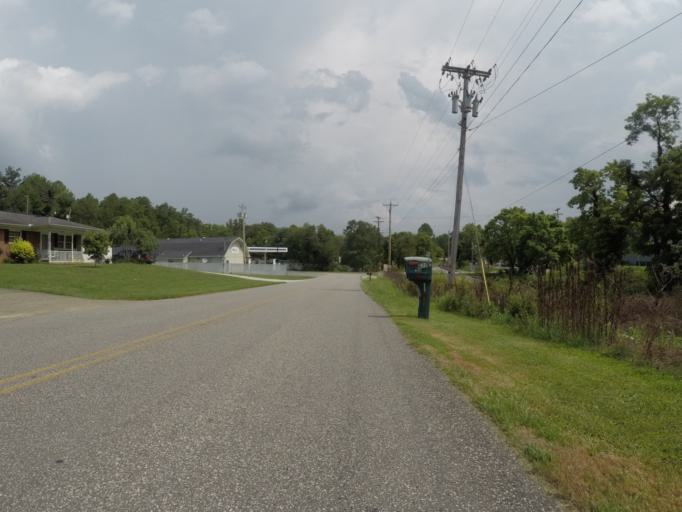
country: US
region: Kentucky
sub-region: Boyd County
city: Ironville
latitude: 38.4396
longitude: -82.7076
